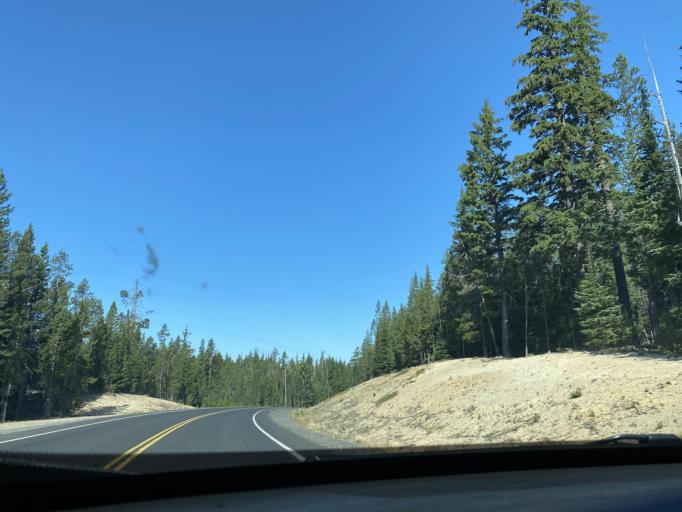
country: US
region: Oregon
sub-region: Deschutes County
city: Three Rivers
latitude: 43.7045
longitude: -121.2620
